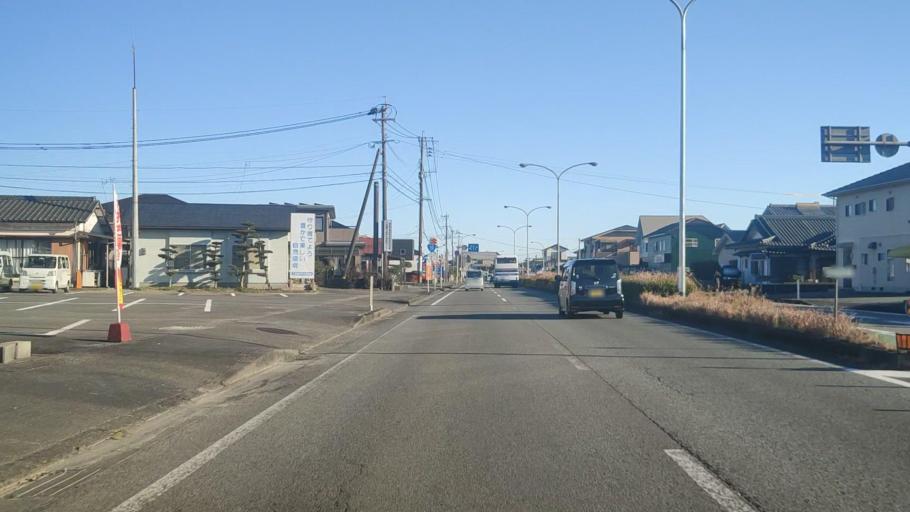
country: JP
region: Miyazaki
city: Nobeoka
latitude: 32.4584
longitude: 131.6459
